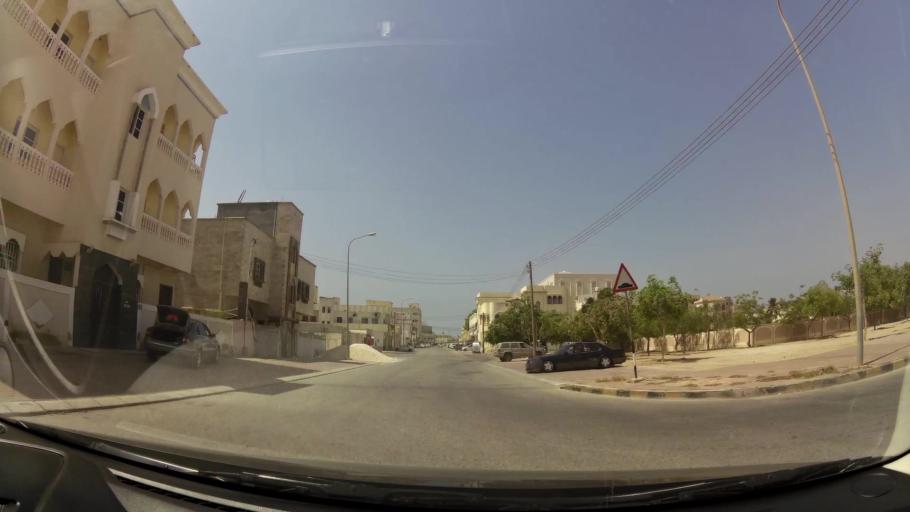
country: OM
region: Zufar
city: Salalah
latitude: 17.0215
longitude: 54.1059
